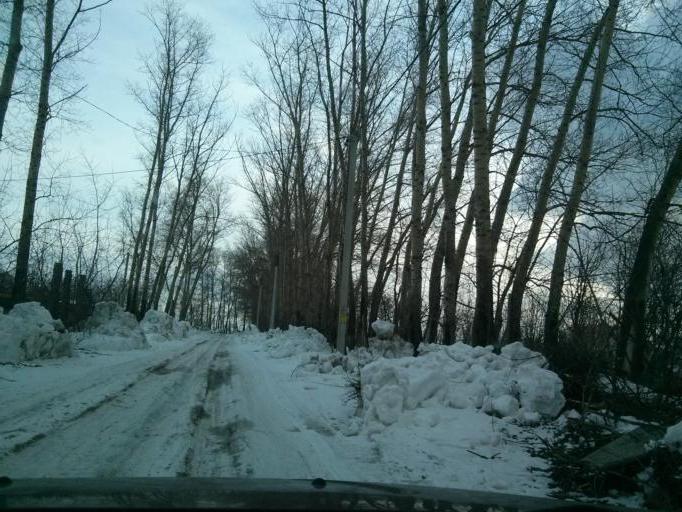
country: RU
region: Nizjnij Novgorod
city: Afonino
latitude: 56.2699
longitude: 44.0318
